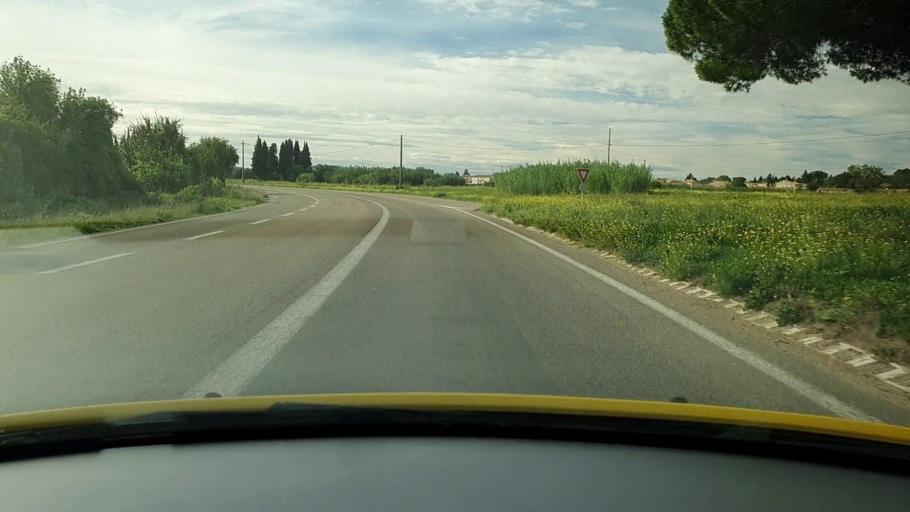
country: FR
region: Languedoc-Roussillon
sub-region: Departement du Gard
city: Bellegarde
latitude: 43.7619
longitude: 4.5251
